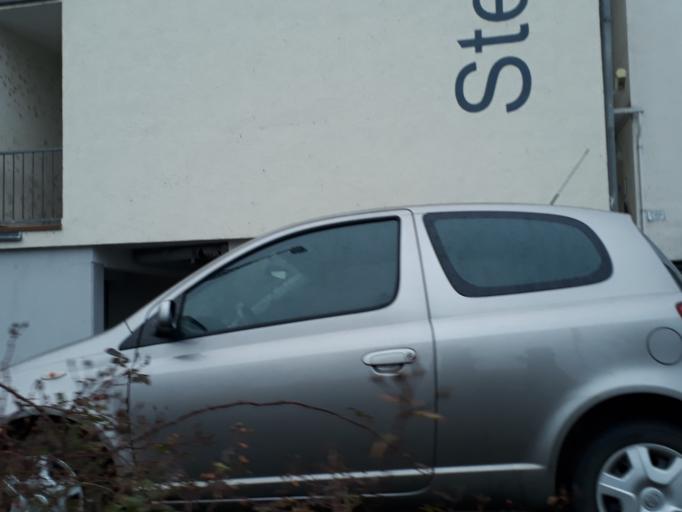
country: DE
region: Hesse
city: Geisenheim
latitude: 49.9809
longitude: 7.9686
